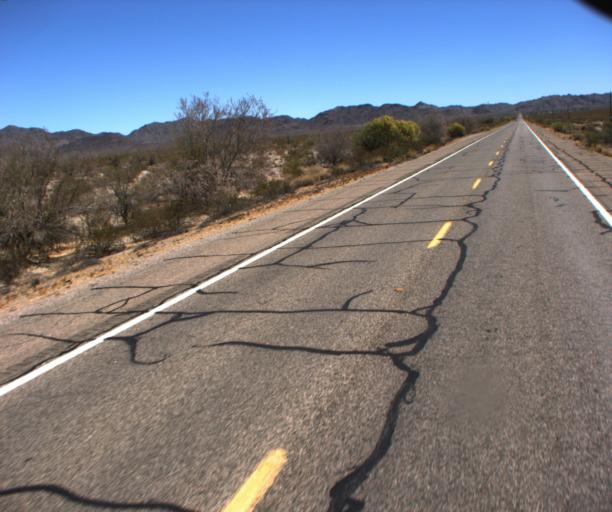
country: US
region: Arizona
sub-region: La Paz County
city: Salome
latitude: 33.7208
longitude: -113.7364
